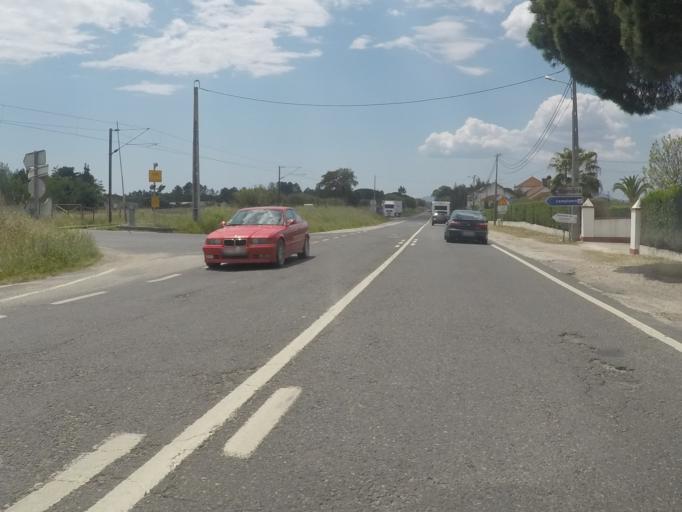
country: PT
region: Setubal
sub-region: Setubal
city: Setubal
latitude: 38.5672
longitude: -8.7726
